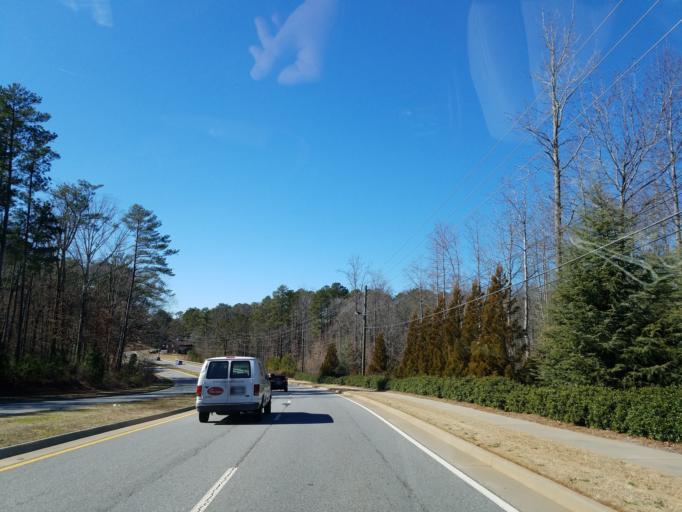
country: US
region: Georgia
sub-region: Fulton County
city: Alpharetta
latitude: 34.0444
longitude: -84.3145
